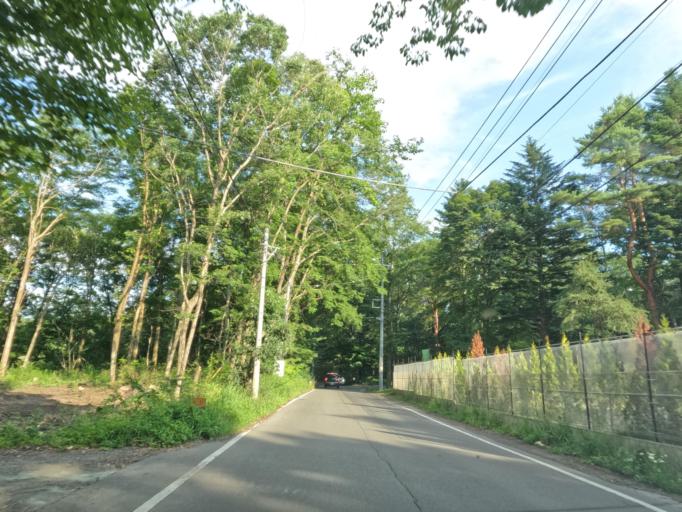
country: JP
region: Nagano
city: Komoro
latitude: 36.4677
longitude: 138.5678
